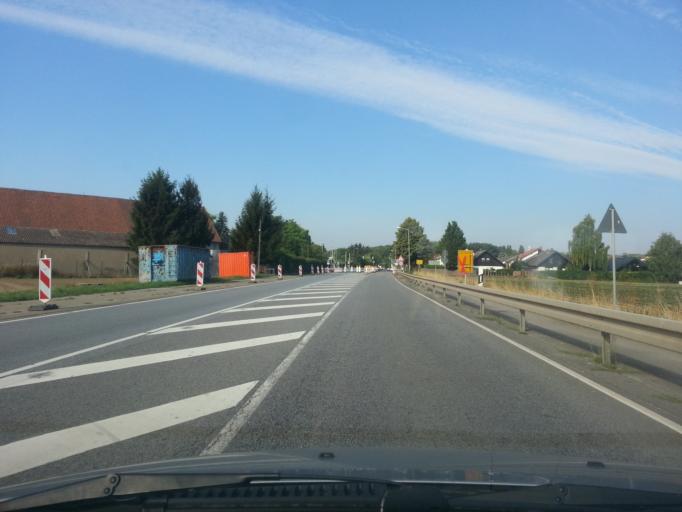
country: DE
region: Rheinland-Pfalz
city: Worms
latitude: 49.6354
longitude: 8.3996
